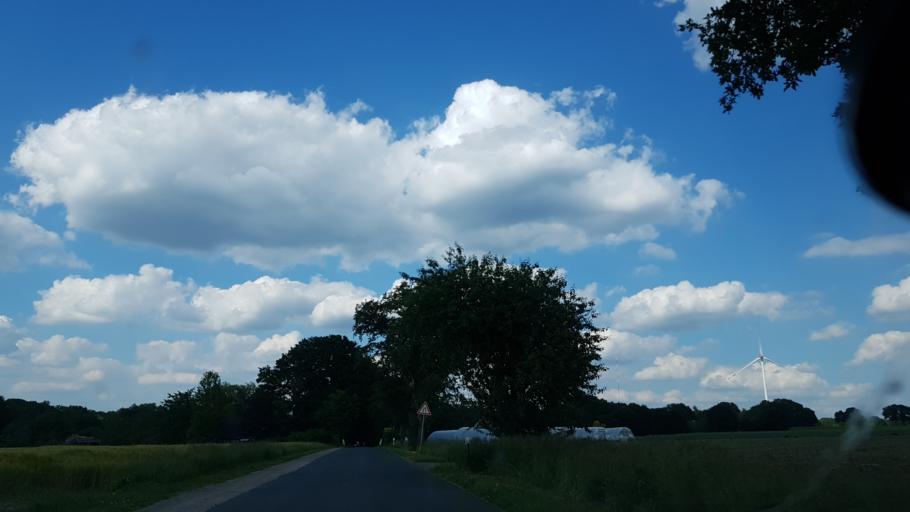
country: DE
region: Lower Saxony
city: Wenzendorf
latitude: 53.3573
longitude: 9.7730
